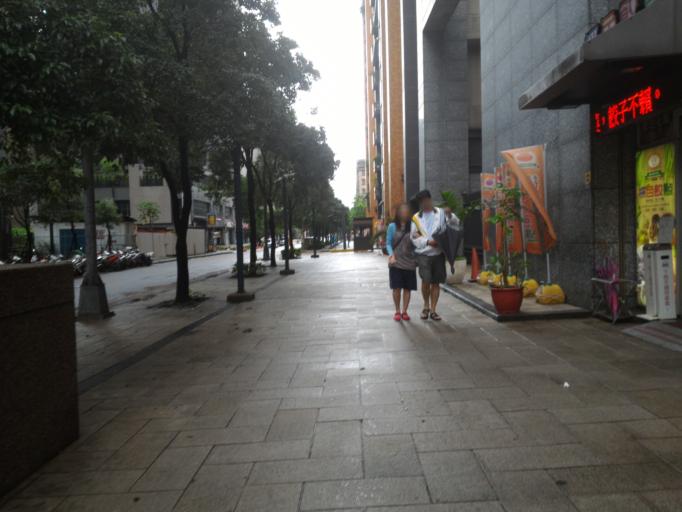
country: TW
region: Taiwan
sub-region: Taoyuan
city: Taoyuan
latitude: 24.9450
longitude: 121.3761
